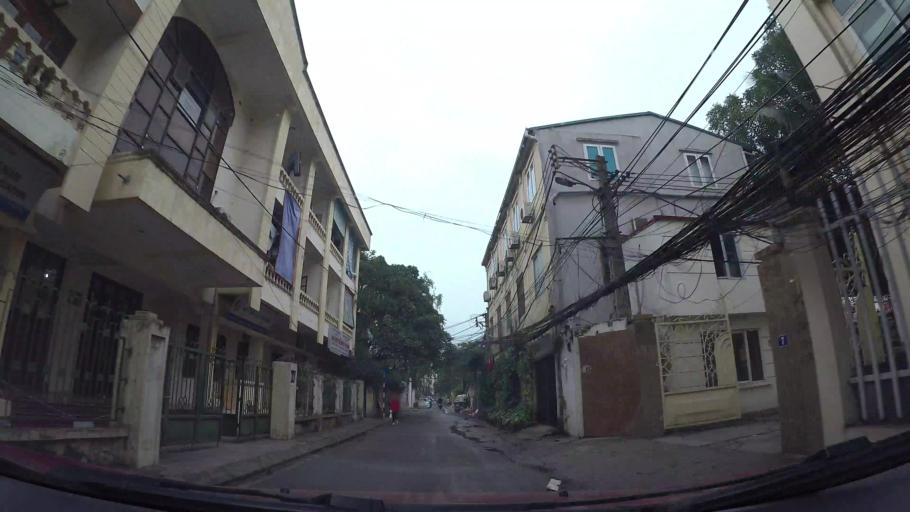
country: VN
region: Ha Noi
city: Dong Da
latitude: 21.0060
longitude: 105.8280
